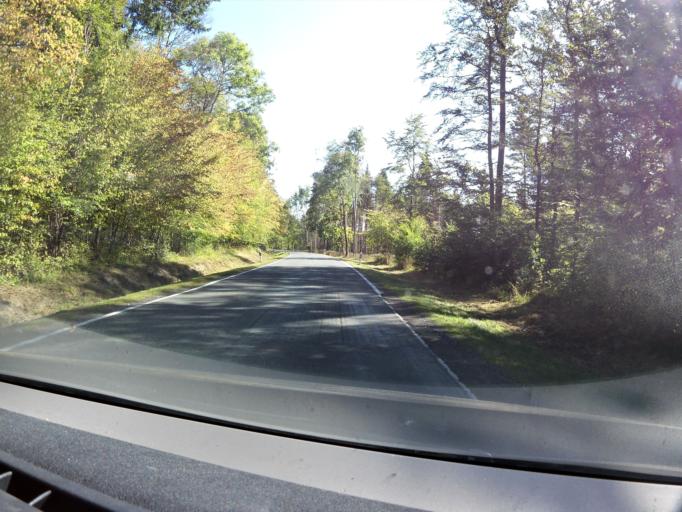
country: DE
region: Saxony-Anhalt
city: Hasselfelde
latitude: 51.6792
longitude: 10.9391
